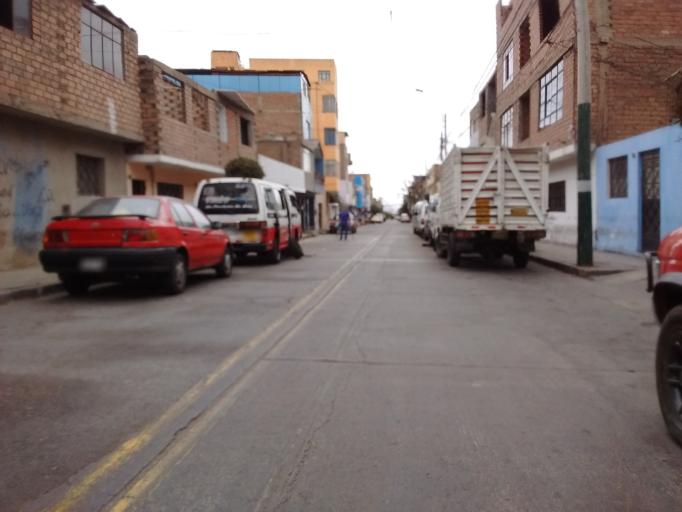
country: PE
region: Callao
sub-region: Callao
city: Callao
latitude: -12.0393
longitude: -77.0924
